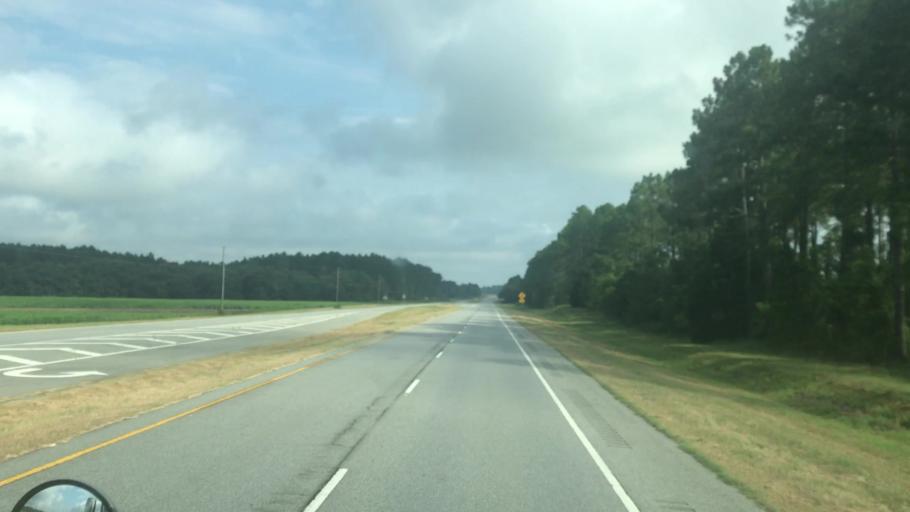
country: US
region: Georgia
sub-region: Miller County
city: Colquitt
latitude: 31.1928
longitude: -84.7659
